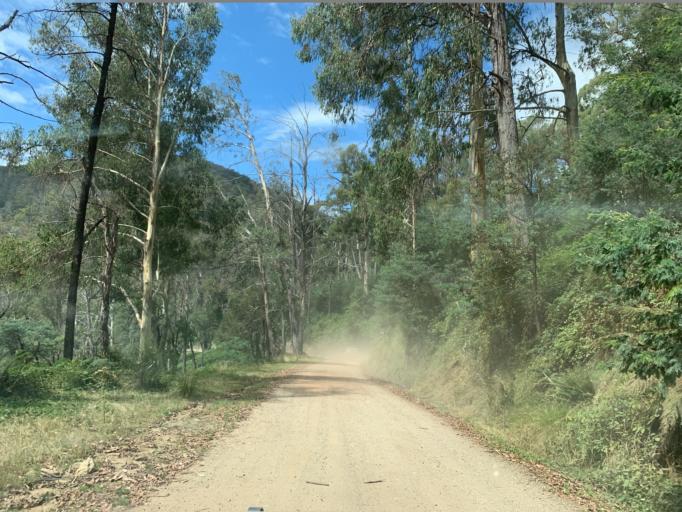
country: AU
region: Victoria
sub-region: Mansfield
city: Mansfield
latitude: -37.1028
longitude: 146.4974
